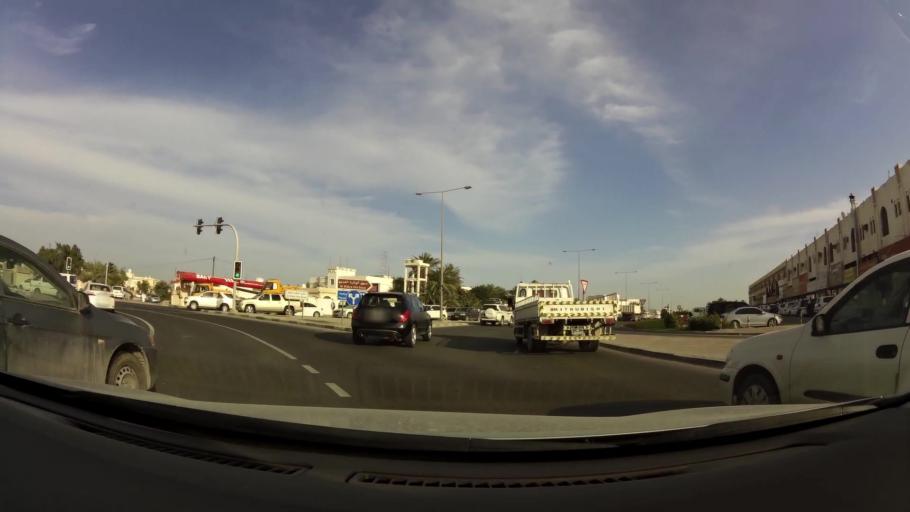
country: QA
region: Al Wakrah
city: Al Wakrah
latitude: 25.1769
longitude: 51.6046
